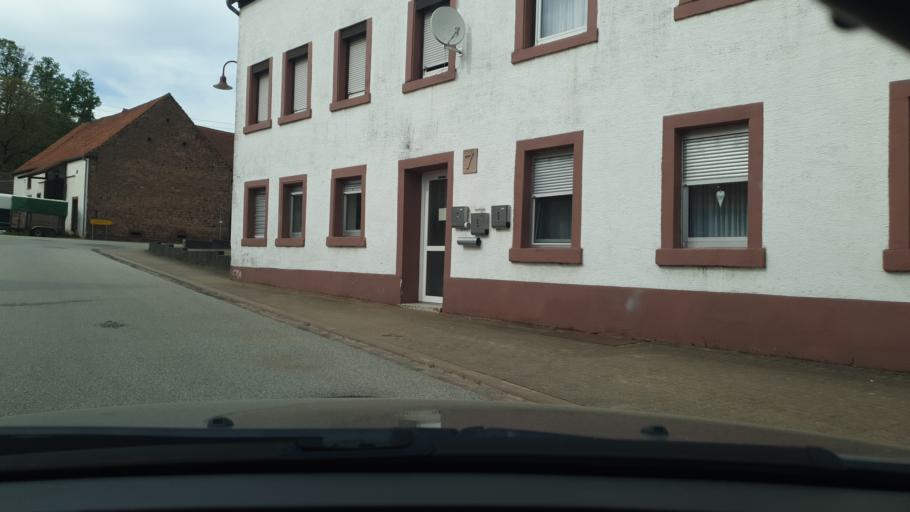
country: DE
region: Rheinland-Pfalz
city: Mittelbrunn
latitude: 49.3738
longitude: 7.5512
